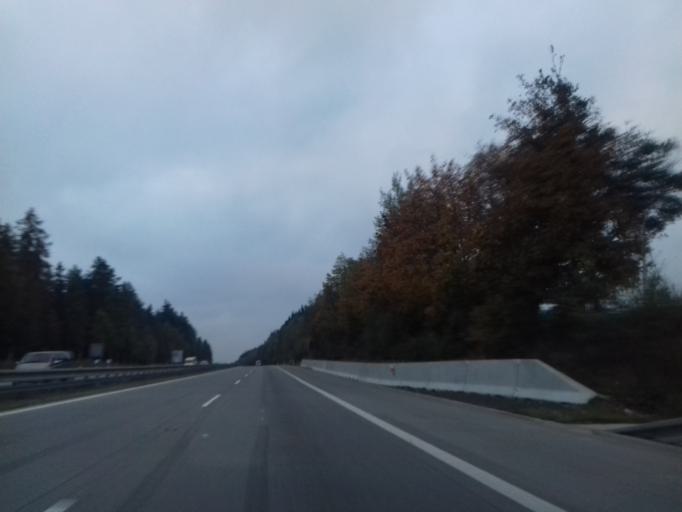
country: CZ
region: Central Bohemia
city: Cechtice
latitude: 49.6353
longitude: 15.1279
